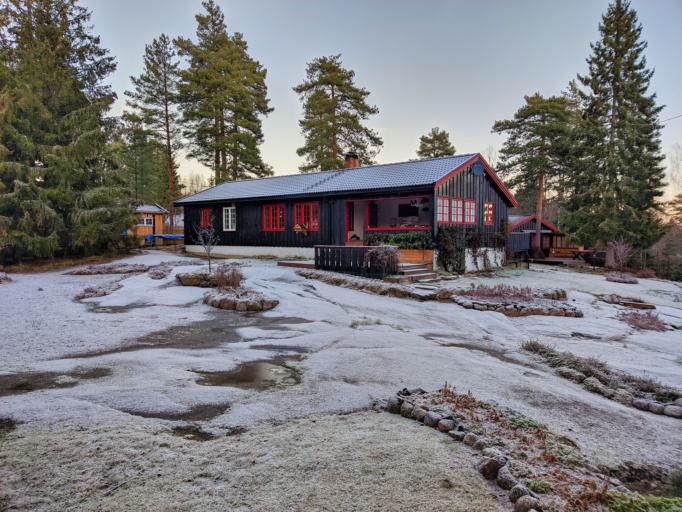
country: NO
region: Akershus
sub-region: Nannestad
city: Teigebyen
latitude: 60.1736
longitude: 10.9810
